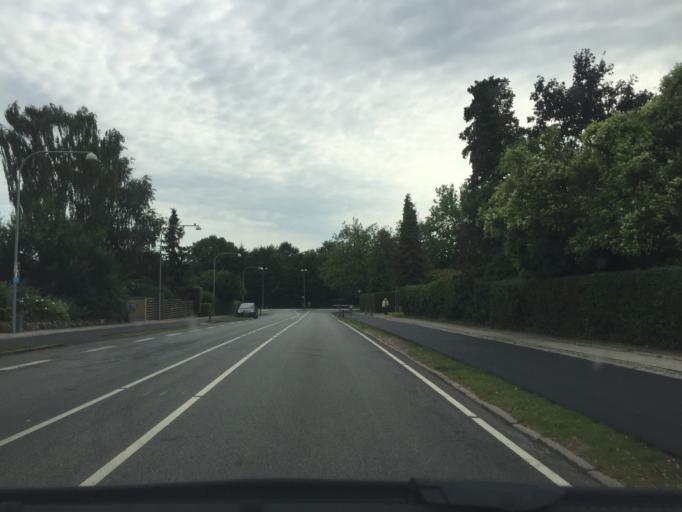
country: DK
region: Capital Region
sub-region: Lyngby-Tarbaek Kommune
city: Kongens Lyngby
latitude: 55.7758
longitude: 12.5362
